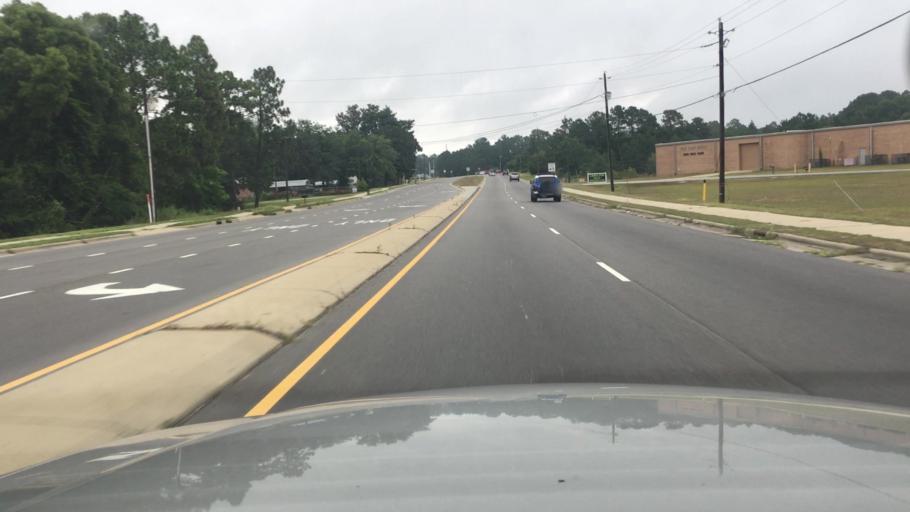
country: US
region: North Carolina
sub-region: Cumberland County
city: Hope Mills
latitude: 34.9843
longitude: -78.9297
